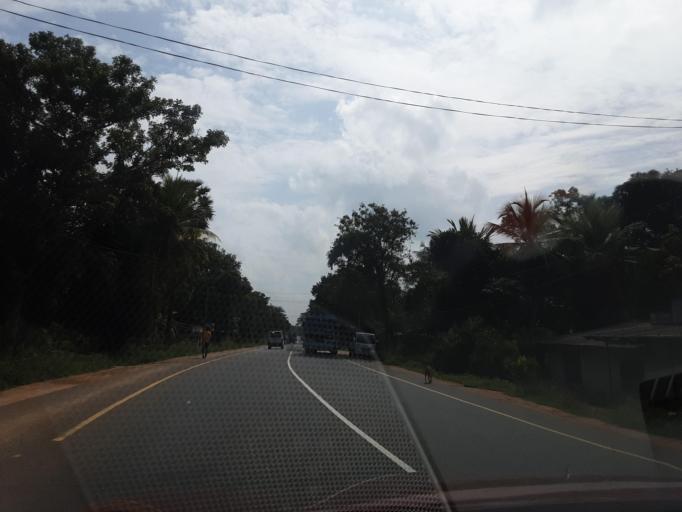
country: LK
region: North Central
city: Anuradhapura
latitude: 8.5016
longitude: 80.5122
